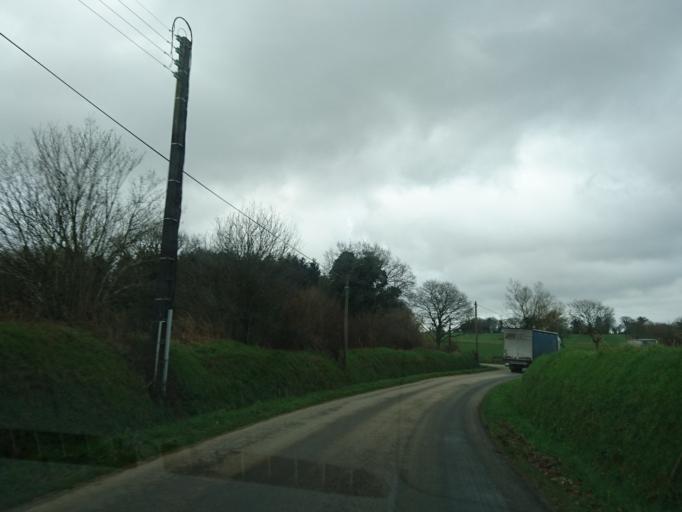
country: FR
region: Brittany
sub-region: Departement des Cotes-d'Armor
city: Glomel
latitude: 48.2221
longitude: -3.3699
